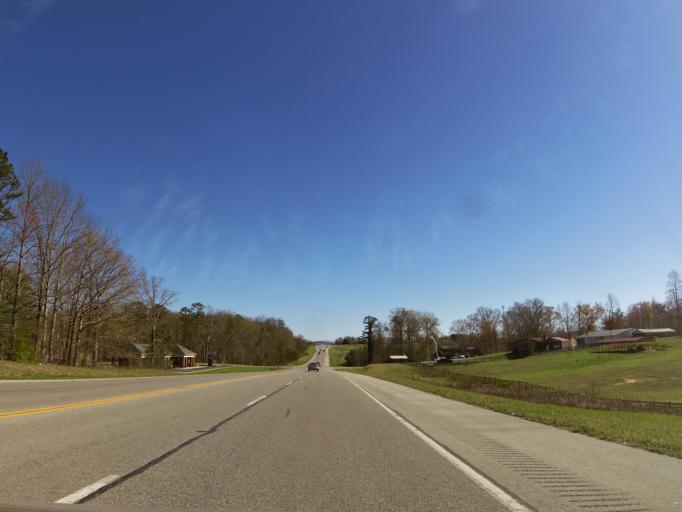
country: US
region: Kentucky
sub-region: McCreary County
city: Pine Knot
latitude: 36.6711
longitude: -84.4429
